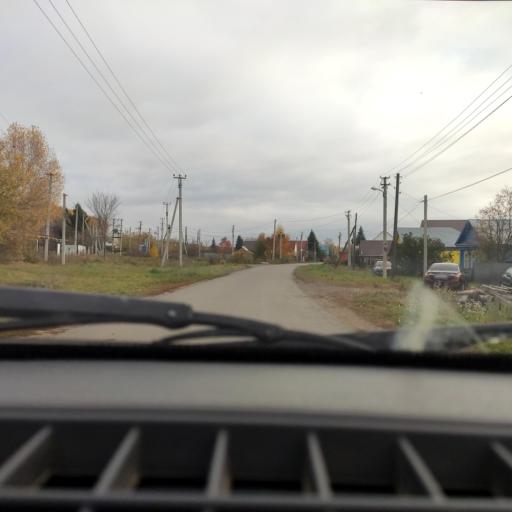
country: RU
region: Bashkortostan
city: Avdon
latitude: 54.6426
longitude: 55.7408
